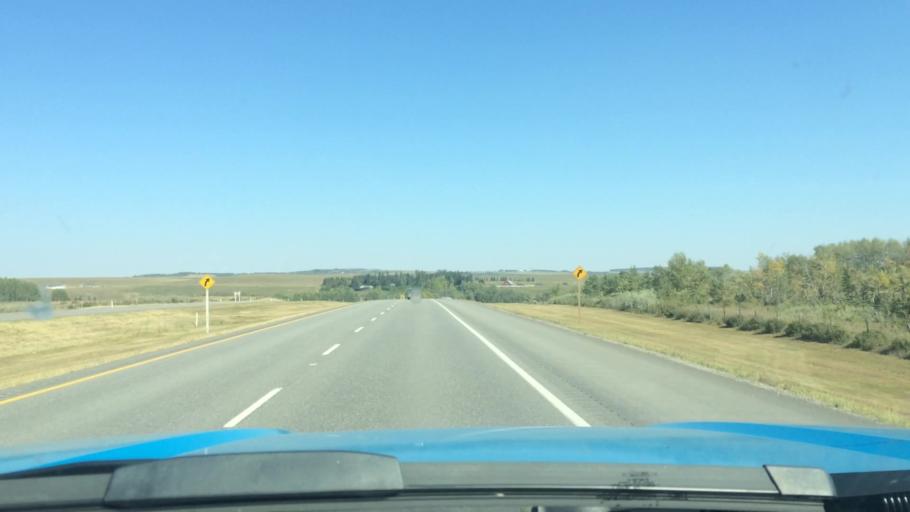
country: CA
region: Alberta
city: Cochrane
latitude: 51.0920
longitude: -114.5574
